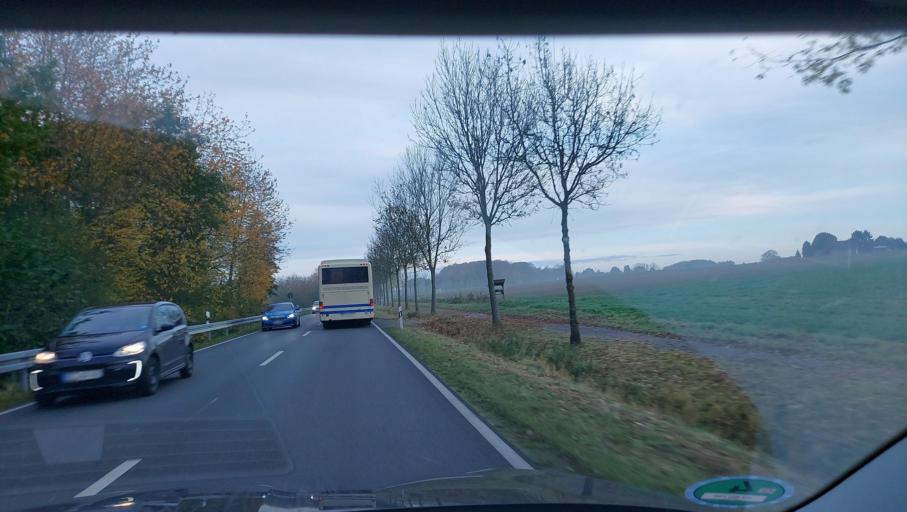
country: DE
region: North Rhine-Westphalia
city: Halle
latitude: 52.0968
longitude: 8.3724
